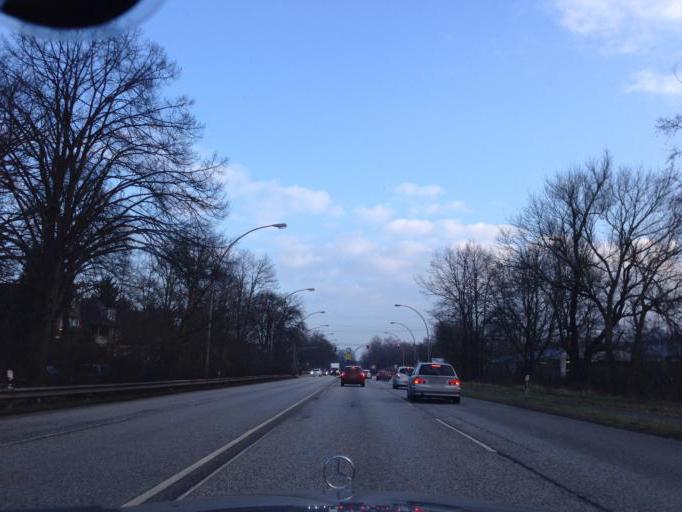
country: DE
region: Schleswig-Holstein
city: Glinde
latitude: 53.5083
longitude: 10.1779
